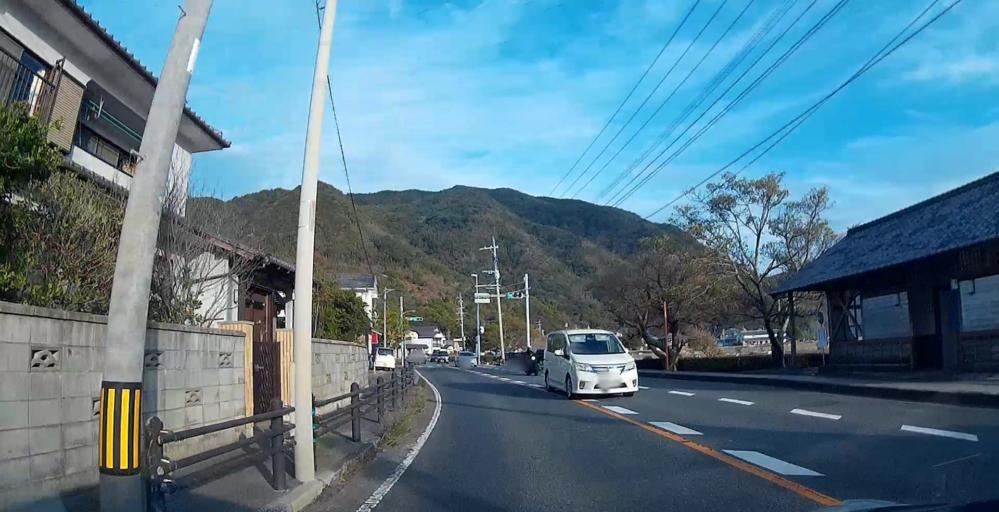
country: JP
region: Nagasaki
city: Shimabara
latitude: 32.6234
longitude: 130.4522
